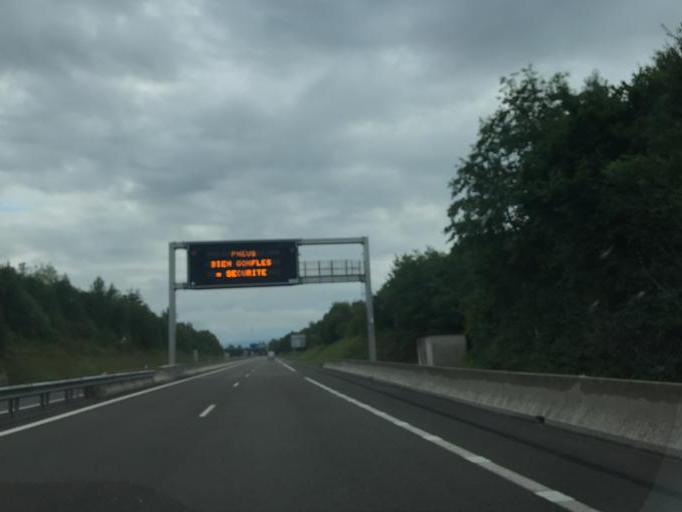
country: FR
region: Rhone-Alpes
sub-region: Departement de l'Ain
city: Groissiat
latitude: 46.2250
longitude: 5.6154
